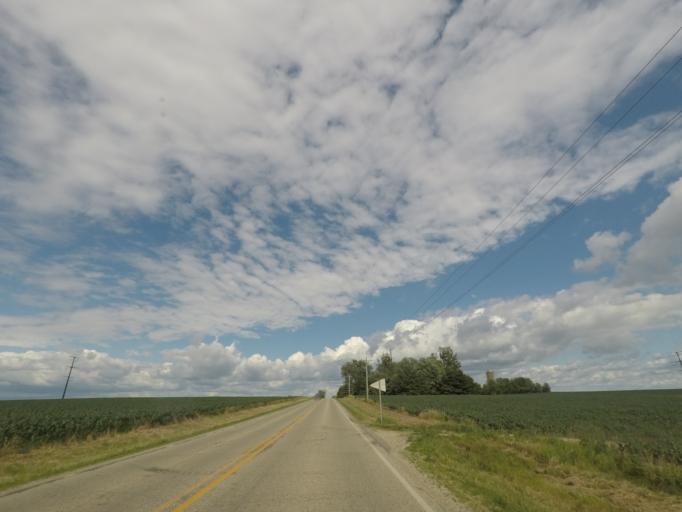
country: US
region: Wisconsin
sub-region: Rock County
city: Janesville
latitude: 42.7012
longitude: -89.1211
